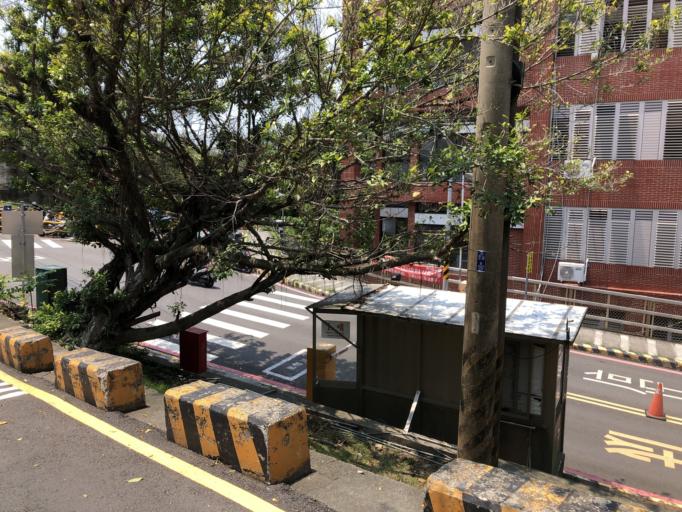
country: TW
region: Kaohsiung
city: Kaohsiung
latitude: 22.6279
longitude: 120.2691
